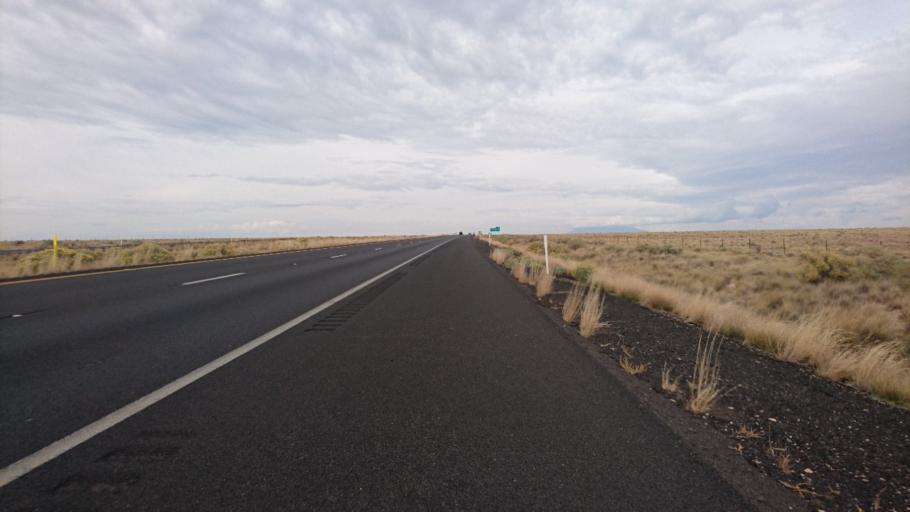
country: US
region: Arizona
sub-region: Coconino County
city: LeChee
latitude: 35.1216
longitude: -111.1597
